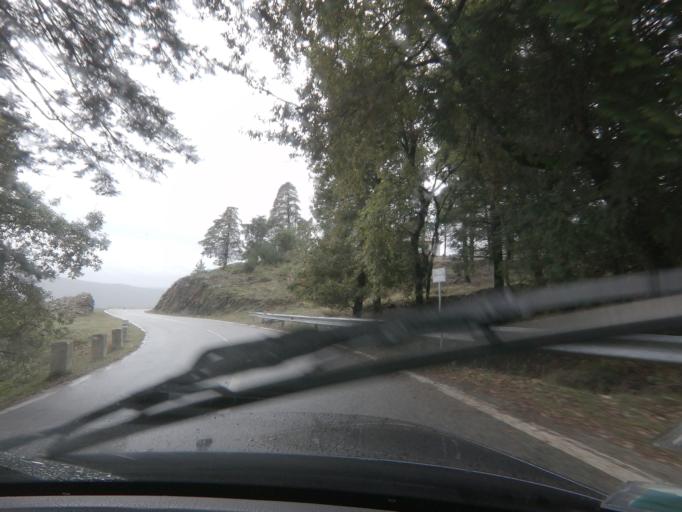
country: PT
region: Vila Real
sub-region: Mondim de Basto
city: Mondim de Basto
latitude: 41.3483
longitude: -7.8754
